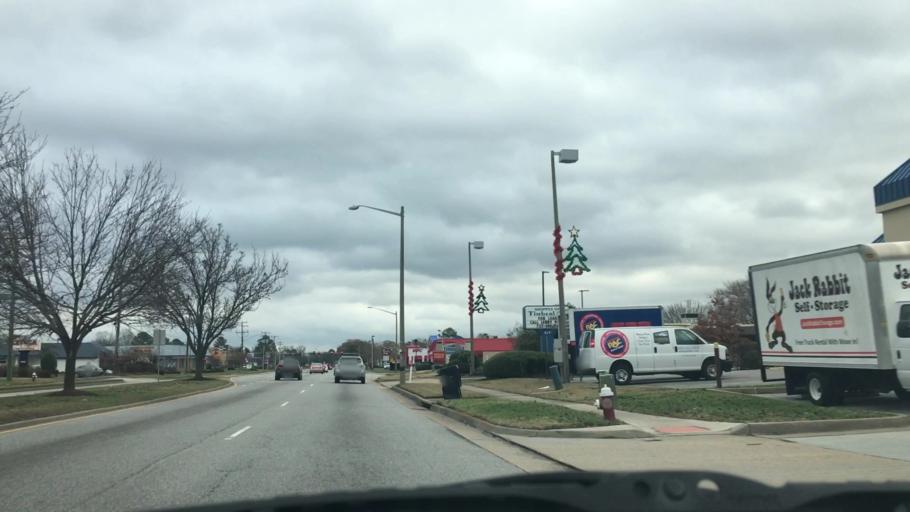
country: US
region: Virginia
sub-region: City of Virginia Beach
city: Virginia Beach
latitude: 36.8211
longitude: -76.1230
